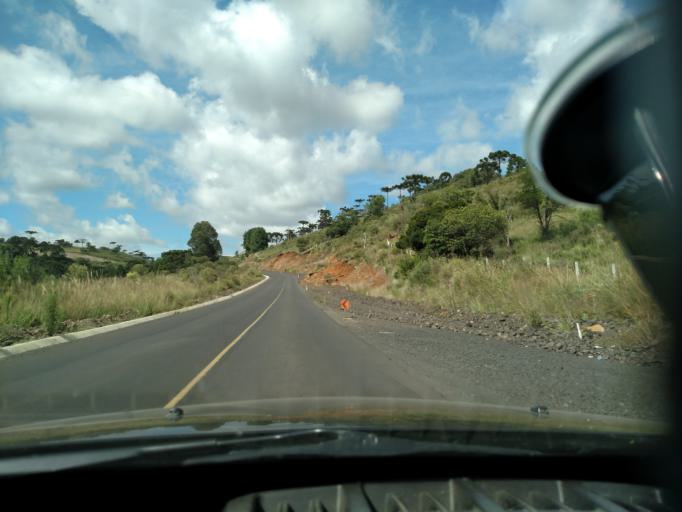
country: BR
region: Santa Catarina
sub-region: Sao Joaquim
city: Sao Joaquim
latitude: -28.1029
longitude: -50.0517
